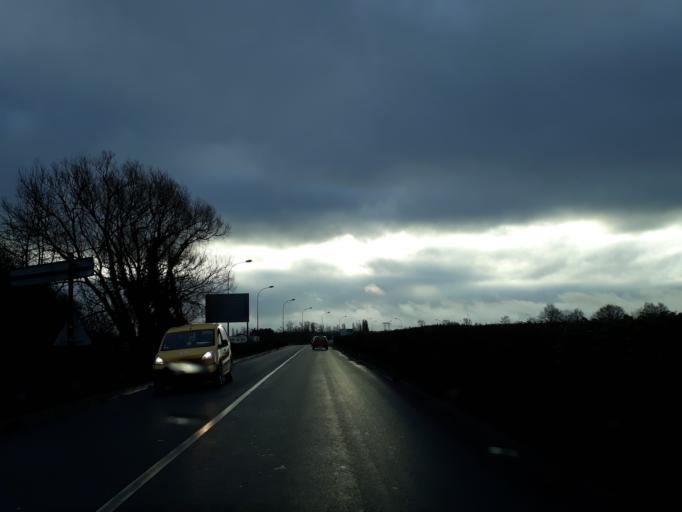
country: FR
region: Ile-de-France
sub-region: Departement de l'Essonne
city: Gometz-la-Ville
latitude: 48.6752
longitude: 2.1334
